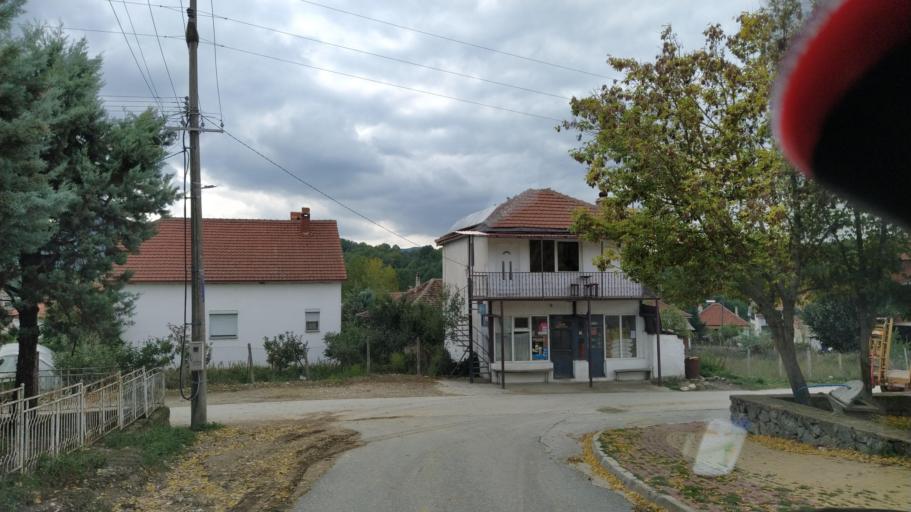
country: MK
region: Konce
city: Konce
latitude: 41.5044
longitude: 22.4574
